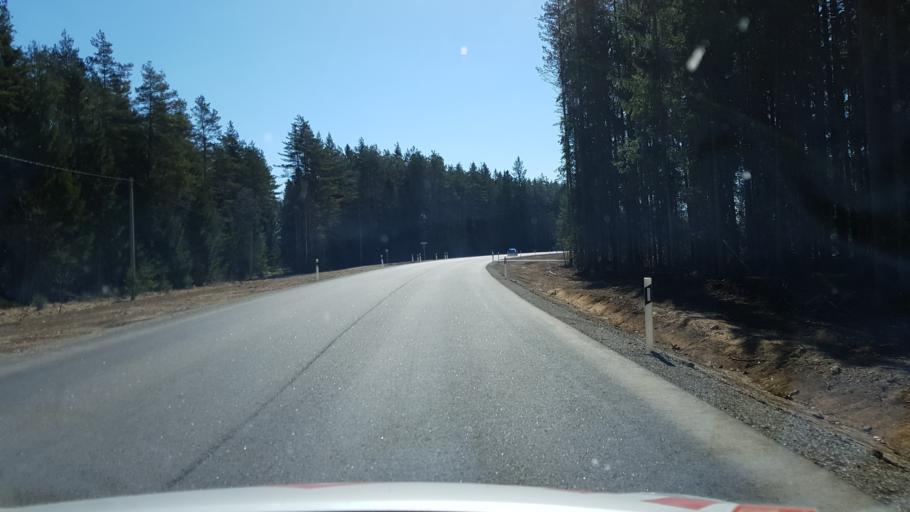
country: EE
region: Laeaene-Virumaa
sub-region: Vinni vald
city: Vinni
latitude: 59.1260
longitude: 26.6149
